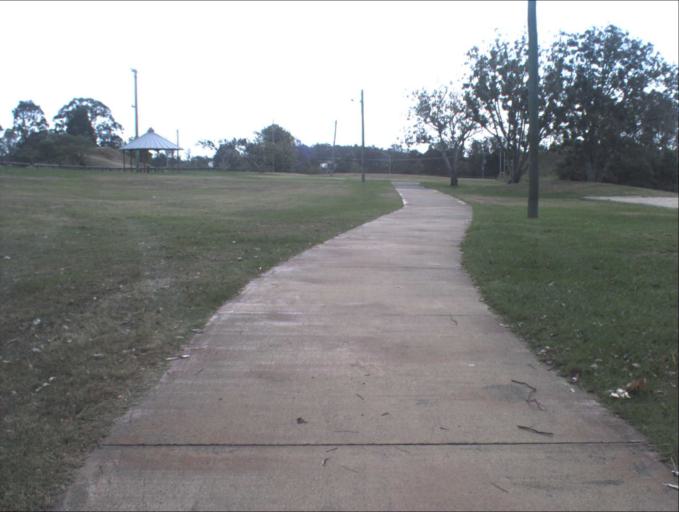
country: AU
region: Queensland
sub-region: Logan
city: Beenleigh
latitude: -27.7062
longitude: 153.1963
